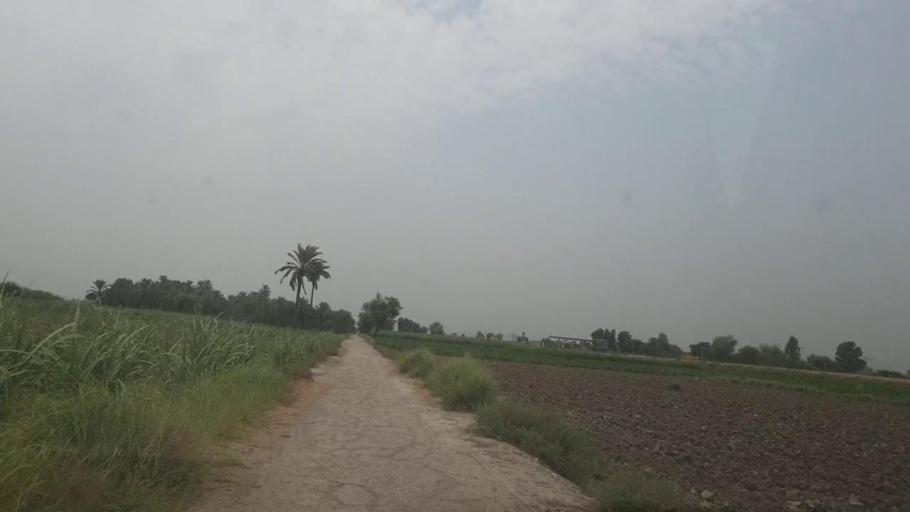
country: PK
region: Sindh
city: Kot Diji
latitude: 27.4261
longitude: 68.6187
